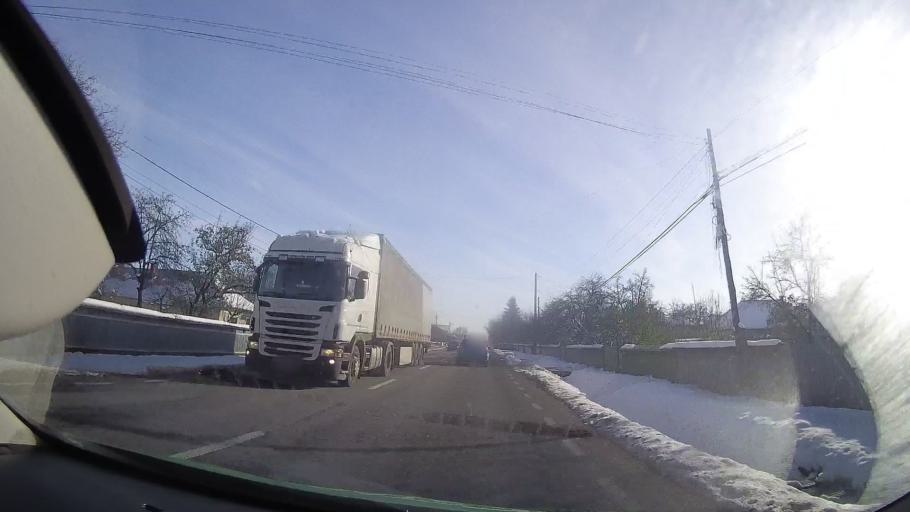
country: RO
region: Neamt
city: Bodesti
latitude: 47.0369
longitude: 26.4102
